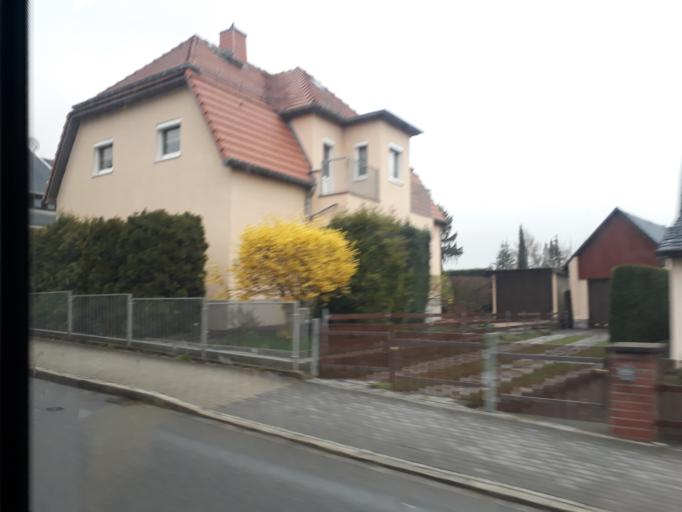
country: DE
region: Saxony
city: Dohna
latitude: 50.9895
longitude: 13.8027
